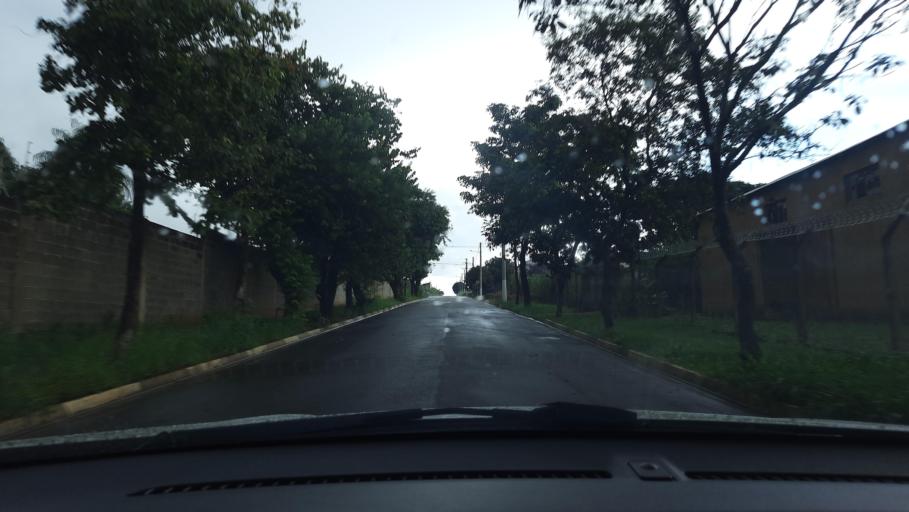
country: BR
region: Sao Paulo
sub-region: Casa Branca
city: Casa Branca
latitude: -21.7530
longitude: -47.0728
